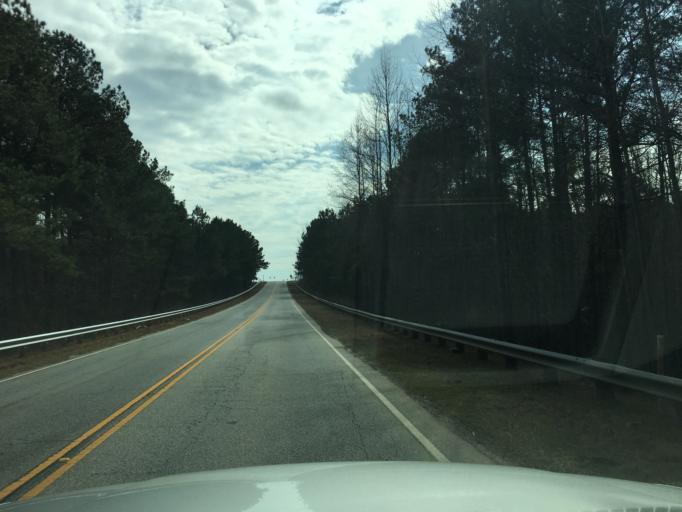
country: US
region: South Carolina
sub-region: Laurens County
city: Clinton
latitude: 34.4886
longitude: -81.8614
